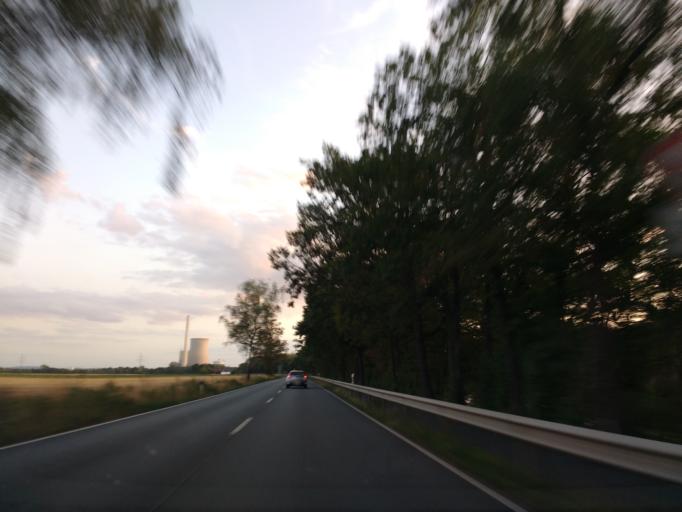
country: DE
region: North Rhine-Westphalia
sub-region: Regierungsbezirk Detmold
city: Petershagen
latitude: 52.3998
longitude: 9.0111
